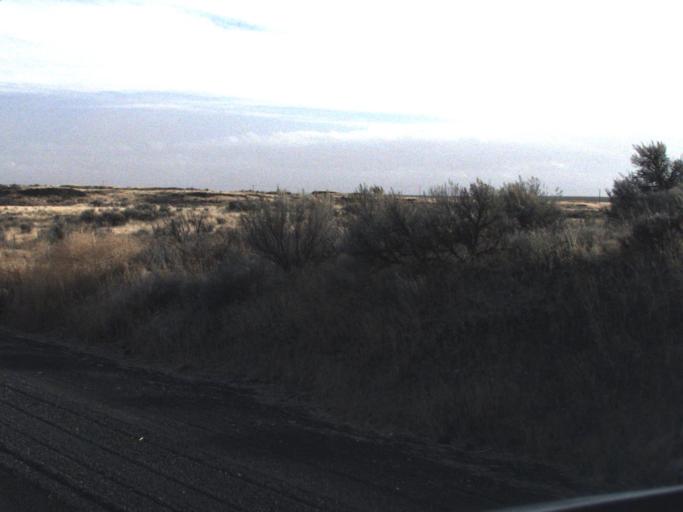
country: US
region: Washington
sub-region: Grant County
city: Warden
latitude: 47.3248
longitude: -118.8679
